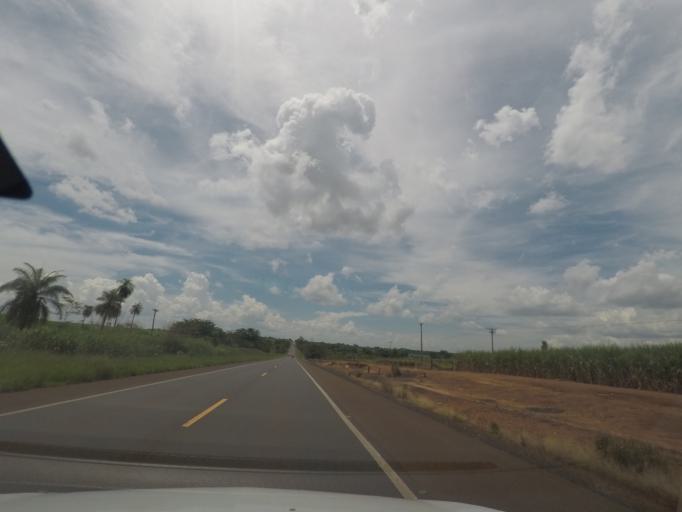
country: BR
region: Sao Paulo
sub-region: Barretos
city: Barretos
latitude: -20.3727
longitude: -48.6450
